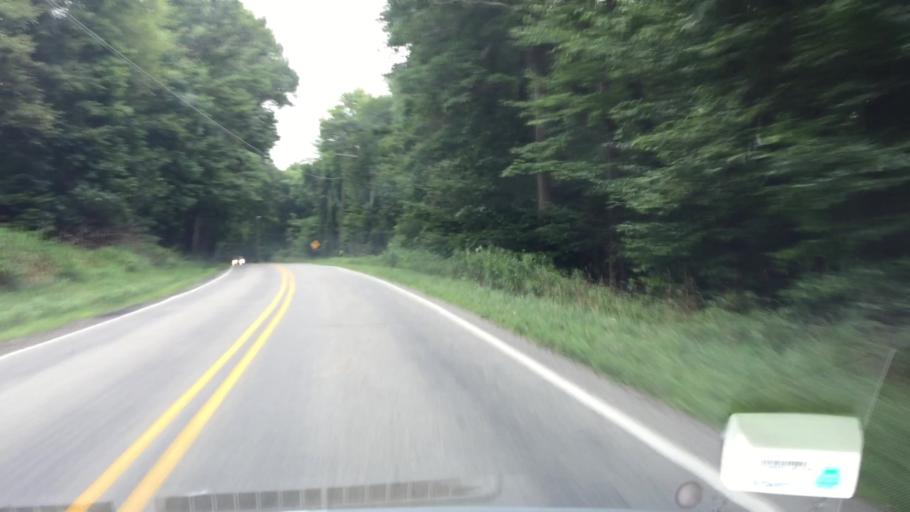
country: US
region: Pennsylvania
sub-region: Allegheny County
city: Curtisville
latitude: 40.7024
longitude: -79.8471
